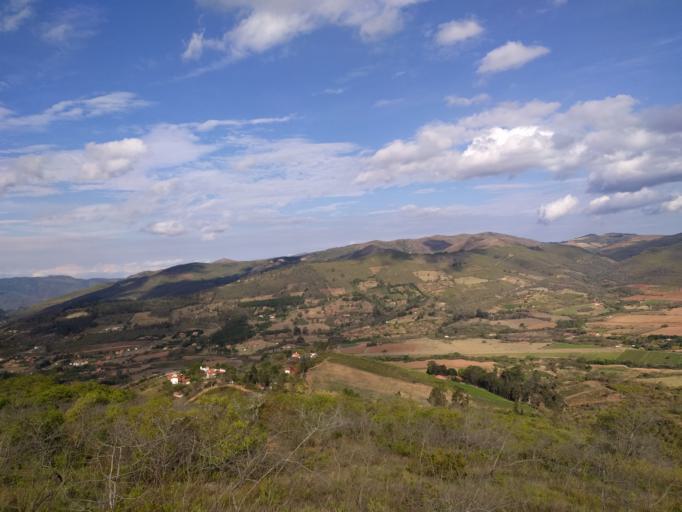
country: BO
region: Santa Cruz
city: Samaipata
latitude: -18.1892
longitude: -63.8888
